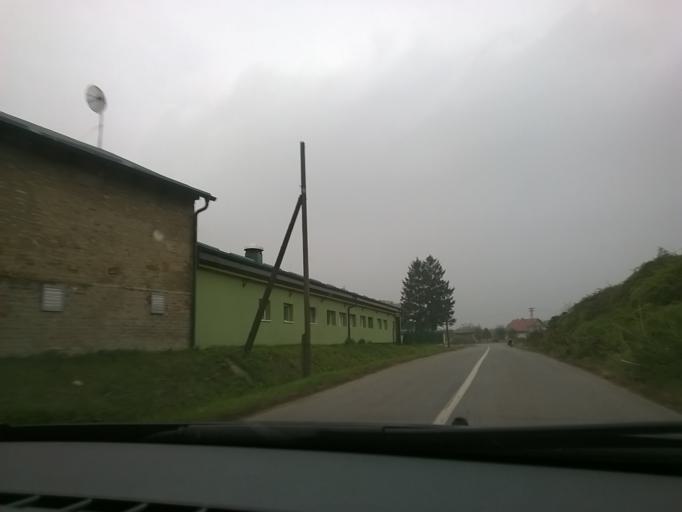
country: RS
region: Autonomna Pokrajina Vojvodina
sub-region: Juznobanatski Okrug
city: Kovin
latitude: 44.8742
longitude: 20.9815
